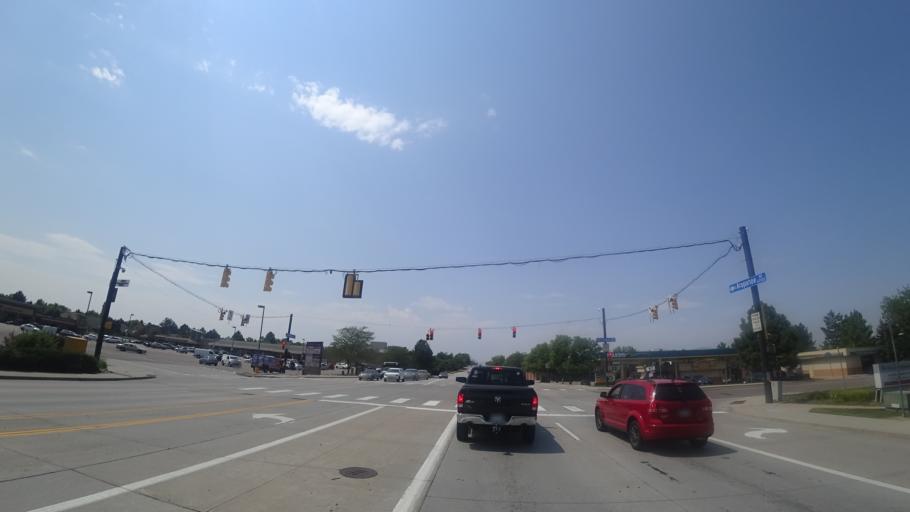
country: US
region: Colorado
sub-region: Arapahoe County
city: Southglenn
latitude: 39.5951
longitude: -104.9269
